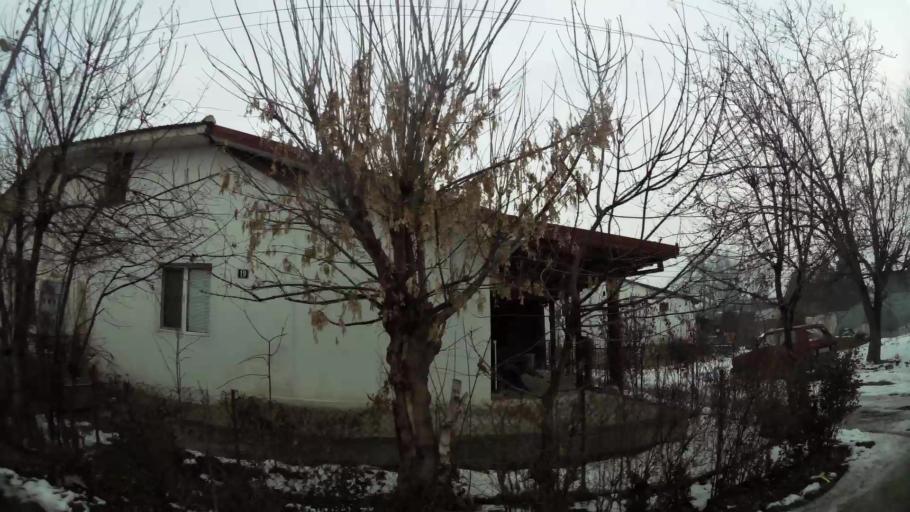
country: MK
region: Ilinden
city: Jurumleri
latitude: 41.9623
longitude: 21.5636
